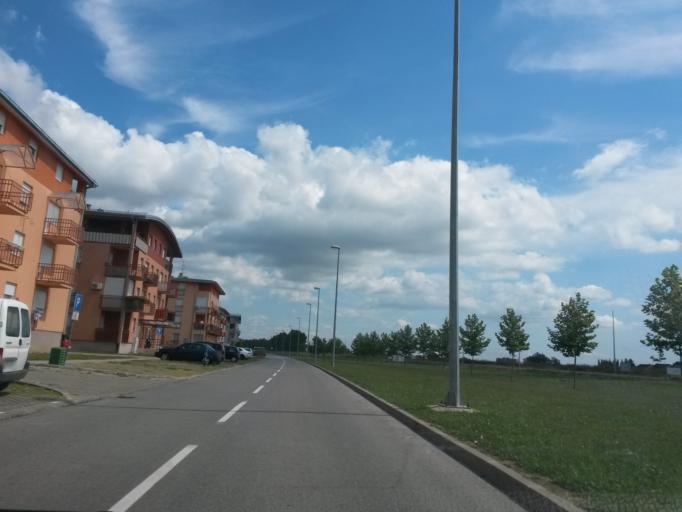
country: HR
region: Osjecko-Baranjska
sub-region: Grad Osijek
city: Osijek
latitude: 45.5409
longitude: 18.6981
